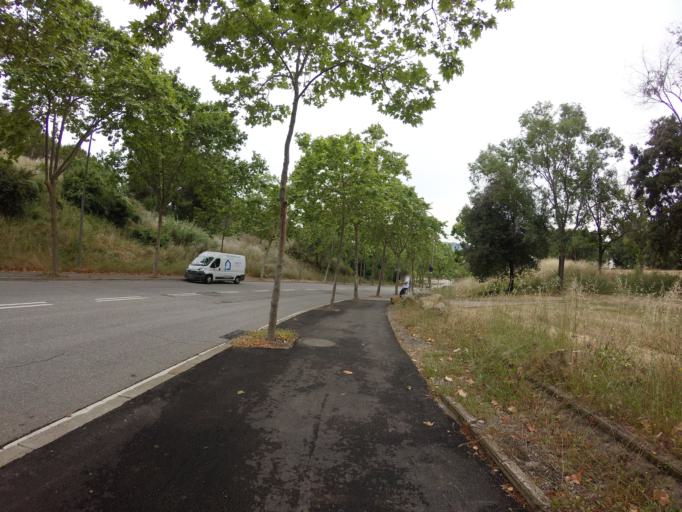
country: ES
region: Catalonia
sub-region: Provincia de Barcelona
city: Sants-Montjuic
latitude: 41.3592
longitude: 2.1539
